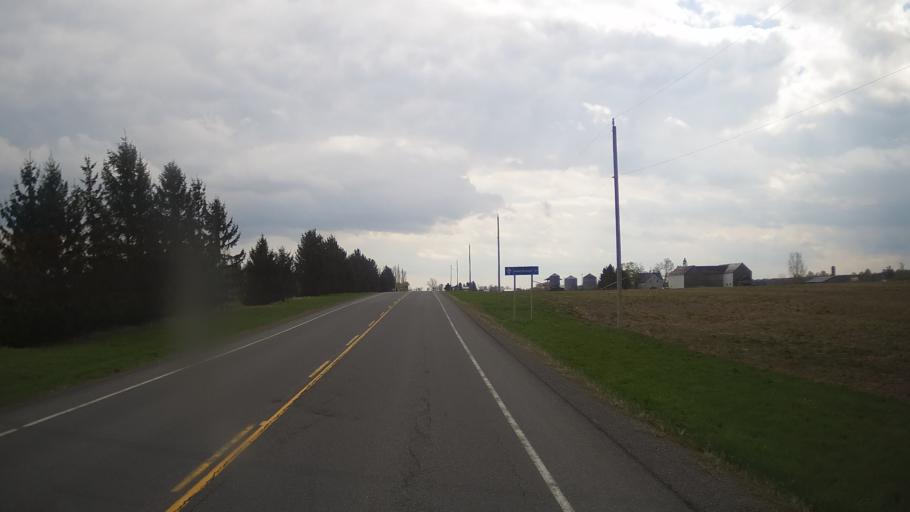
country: CA
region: Ontario
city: Hawkesbury
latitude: 45.5414
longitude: -74.5502
